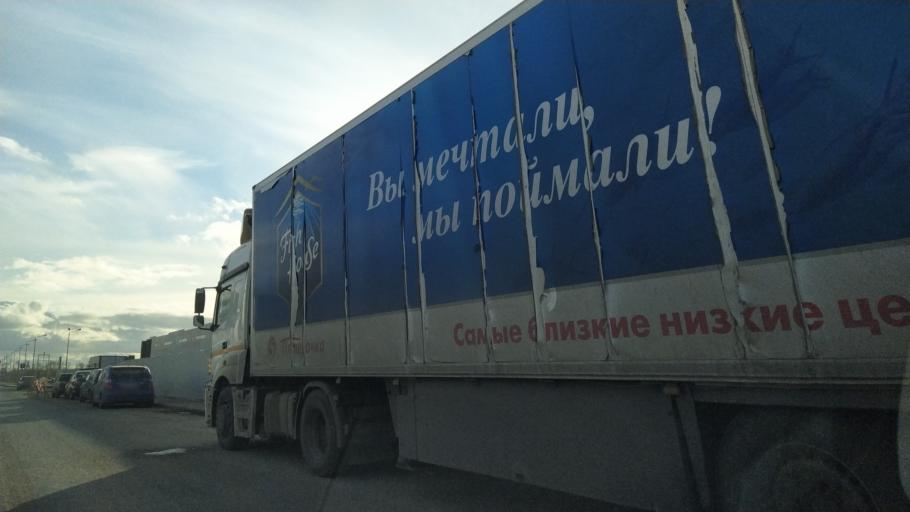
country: RU
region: St.-Petersburg
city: Petro-Slavyanka
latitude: 59.7758
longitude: 30.4611
